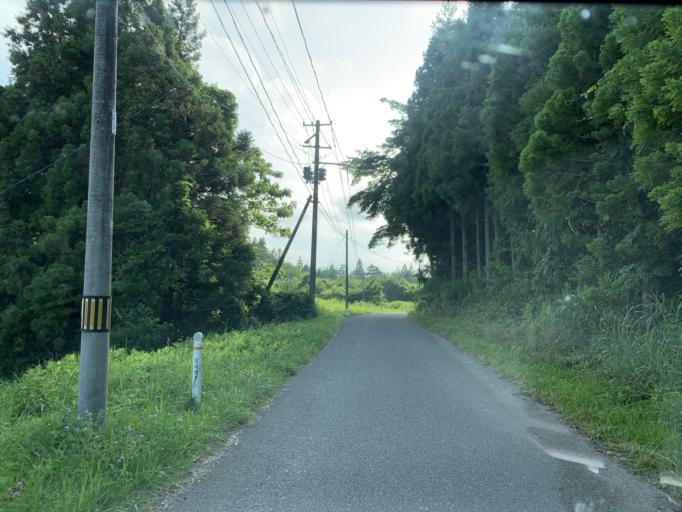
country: JP
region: Iwate
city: Ichinoseki
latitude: 38.8611
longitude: 141.1202
